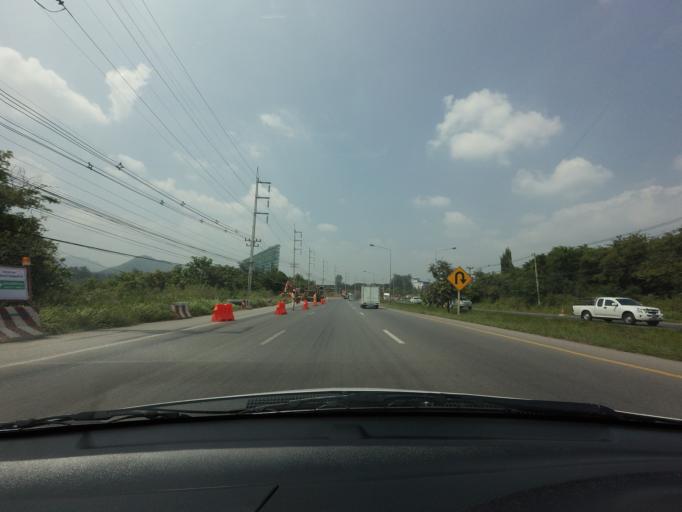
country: TH
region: Nakhon Ratchasima
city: Pak Chong
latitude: 14.6520
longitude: 101.3547
